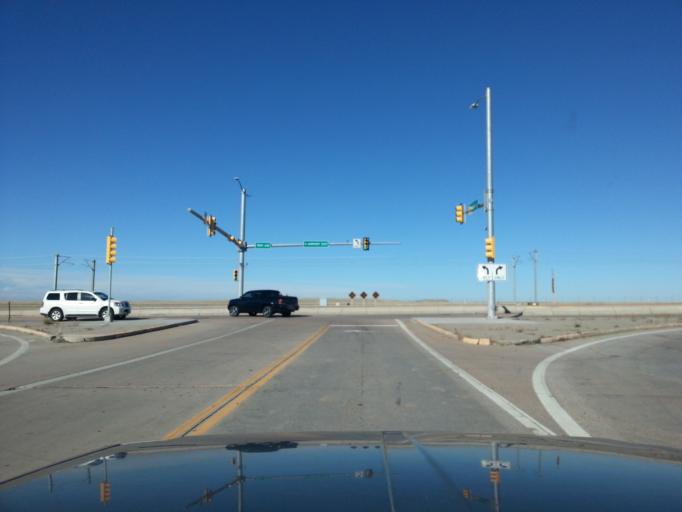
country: US
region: Colorado
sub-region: Adams County
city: Aurora
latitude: 39.8378
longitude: -104.7154
